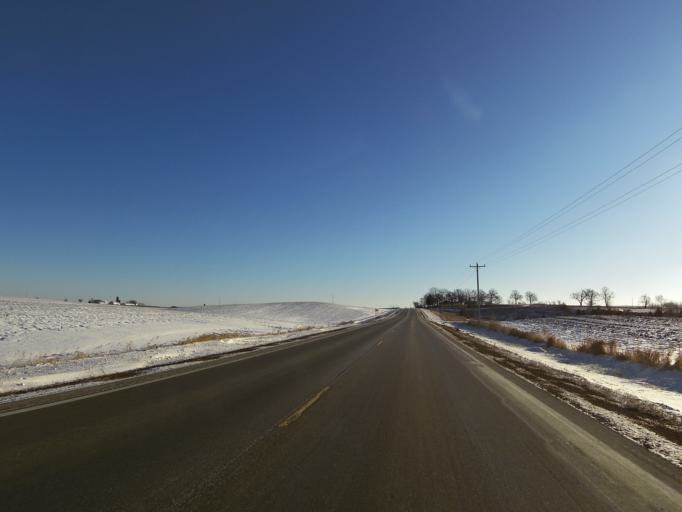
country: US
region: Minnesota
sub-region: Carver County
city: Carver
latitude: 44.7327
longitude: -93.5673
